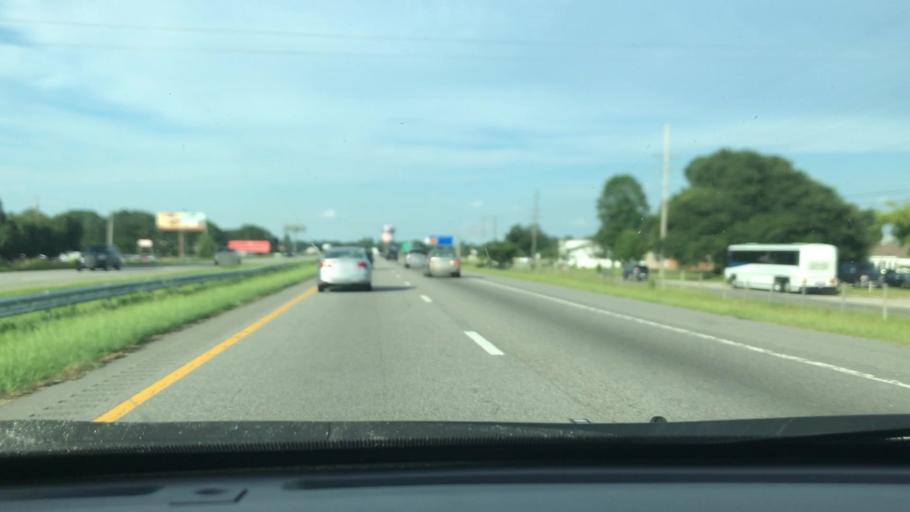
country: US
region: North Carolina
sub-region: Robeson County
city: Lumberton
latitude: 34.6139
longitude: -79.0719
